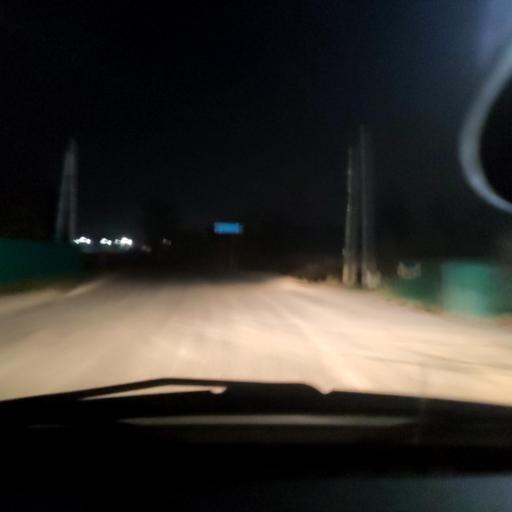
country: RU
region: Bashkortostan
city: Iglino
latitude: 54.8474
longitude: 56.4440
